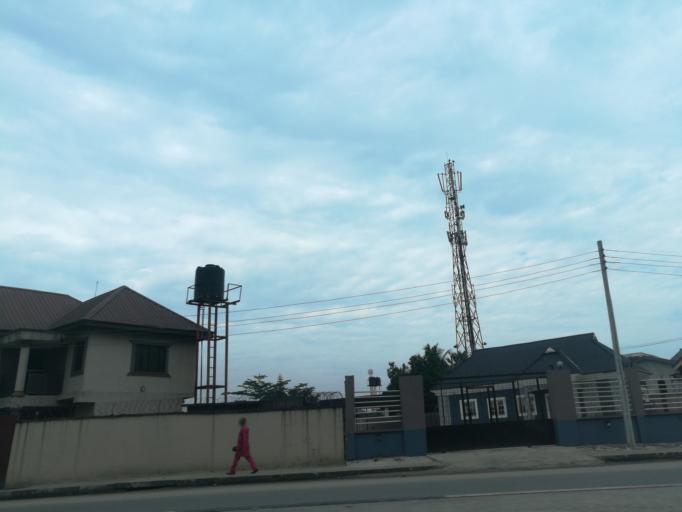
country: NG
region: Rivers
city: Port Harcourt
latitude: 4.8439
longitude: 6.9752
